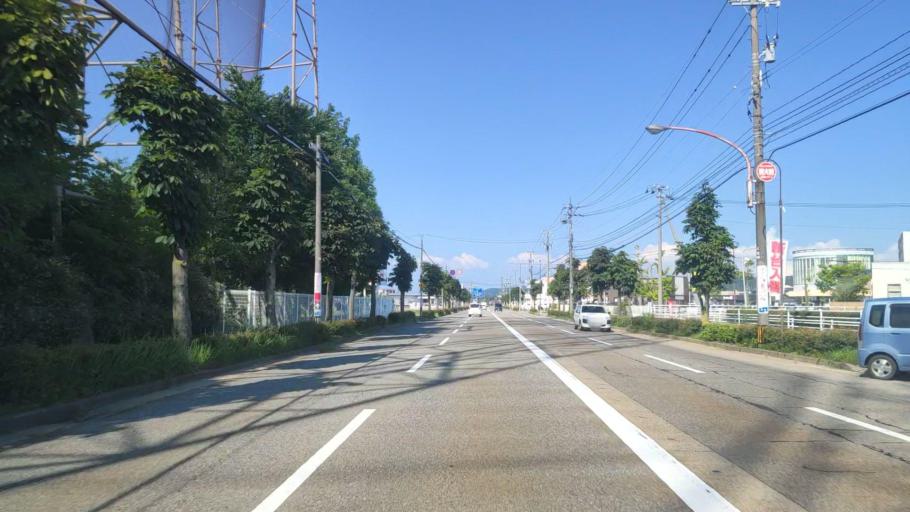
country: JP
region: Ishikawa
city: Kanazawa-shi
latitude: 36.5922
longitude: 136.6592
